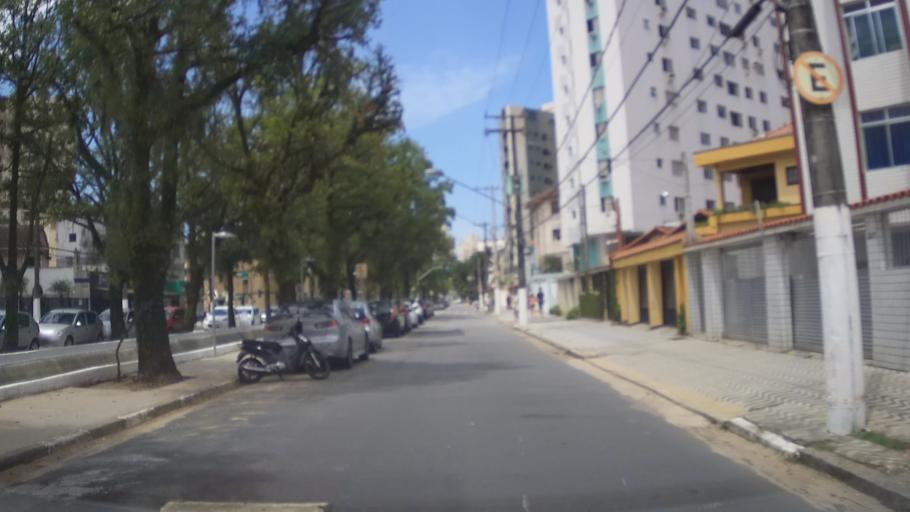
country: BR
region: Sao Paulo
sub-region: Santos
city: Santos
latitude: -23.9593
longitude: -46.3481
